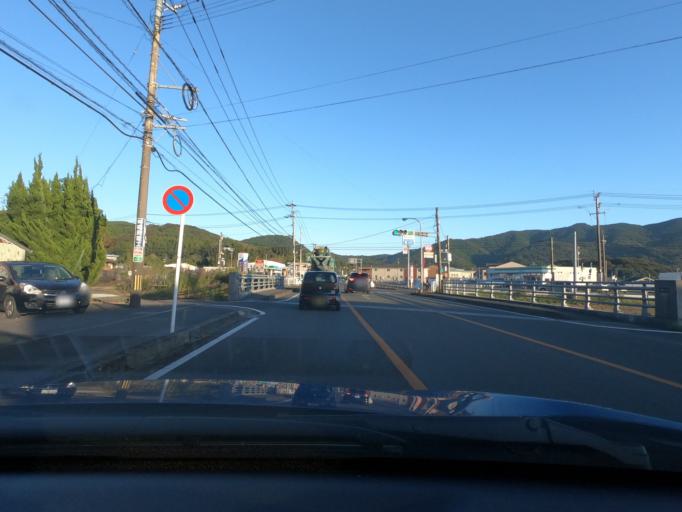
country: JP
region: Kagoshima
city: Satsumasendai
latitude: 31.8069
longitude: 130.3438
